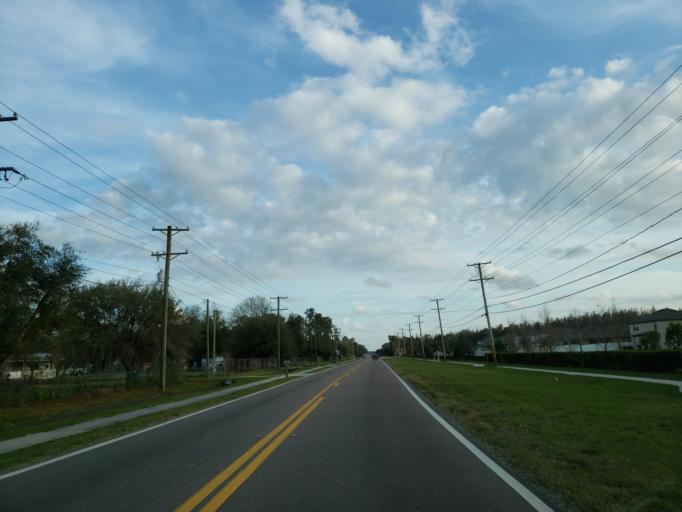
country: US
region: Florida
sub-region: Hillsborough County
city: Riverview
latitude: 27.8180
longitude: -82.2953
